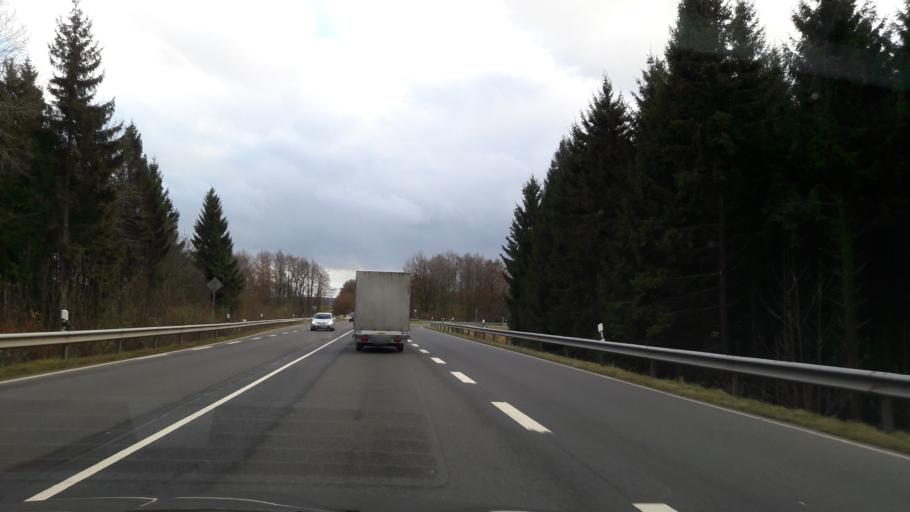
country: DE
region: Rheinland-Pfalz
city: Reinsfeld
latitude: 49.6930
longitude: 6.8834
